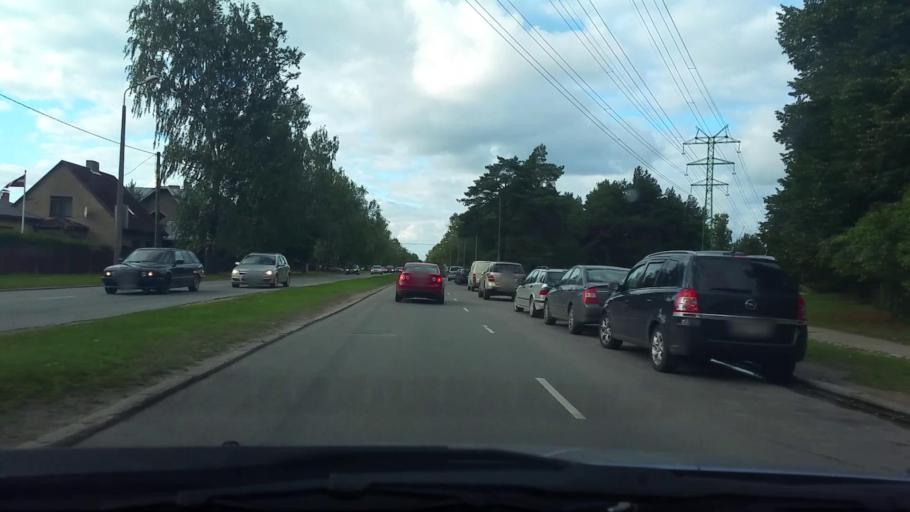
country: LV
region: Riga
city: Jaunciems
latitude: 56.9686
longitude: 24.1956
